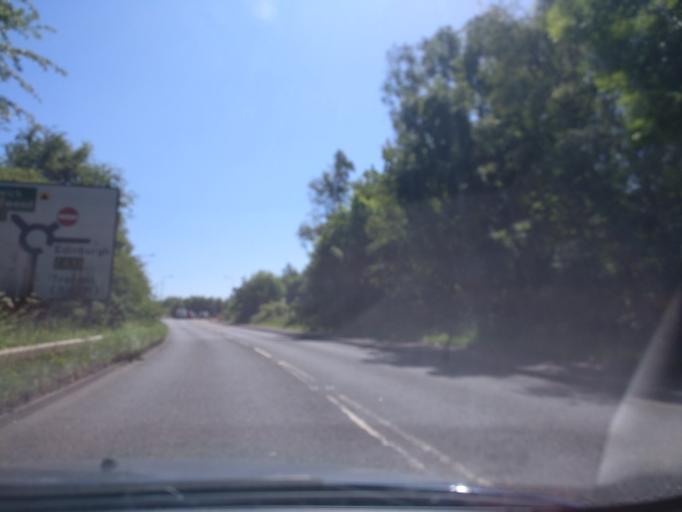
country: GB
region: Scotland
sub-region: East Lothian
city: Tranent
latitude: 55.9550
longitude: -2.9514
